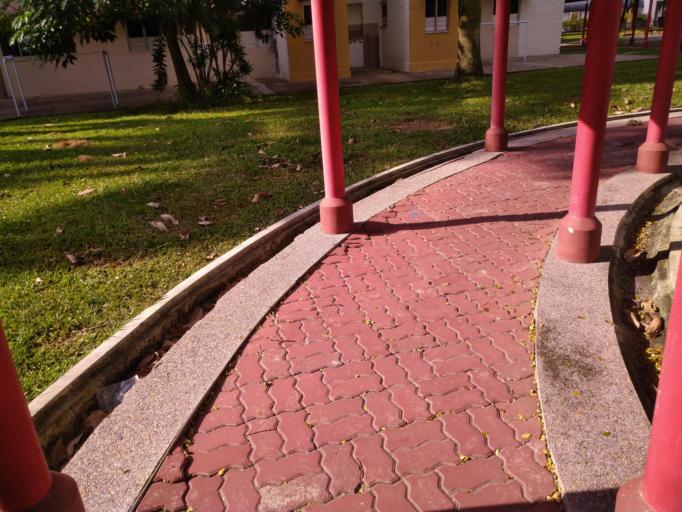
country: SG
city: Singapore
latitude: 1.2853
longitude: 103.8172
